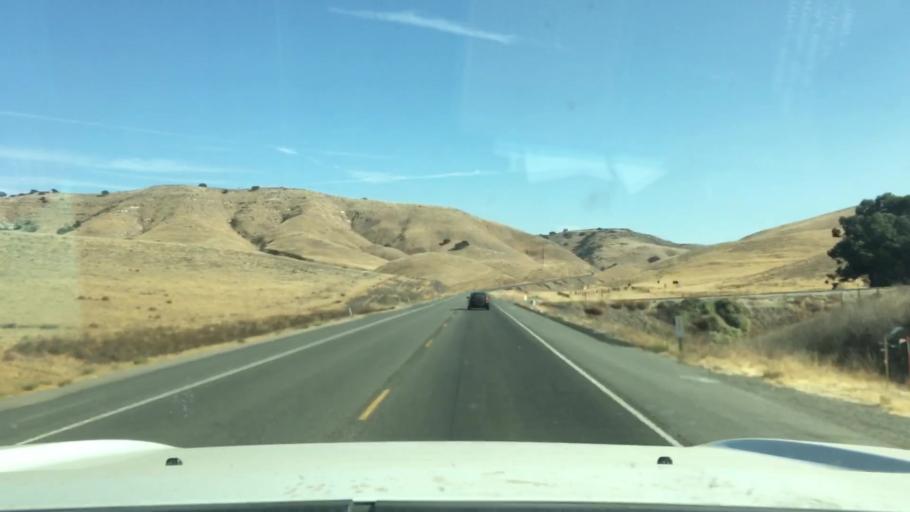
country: US
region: California
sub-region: San Luis Obispo County
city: Shandon
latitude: 35.7436
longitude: -120.2304
